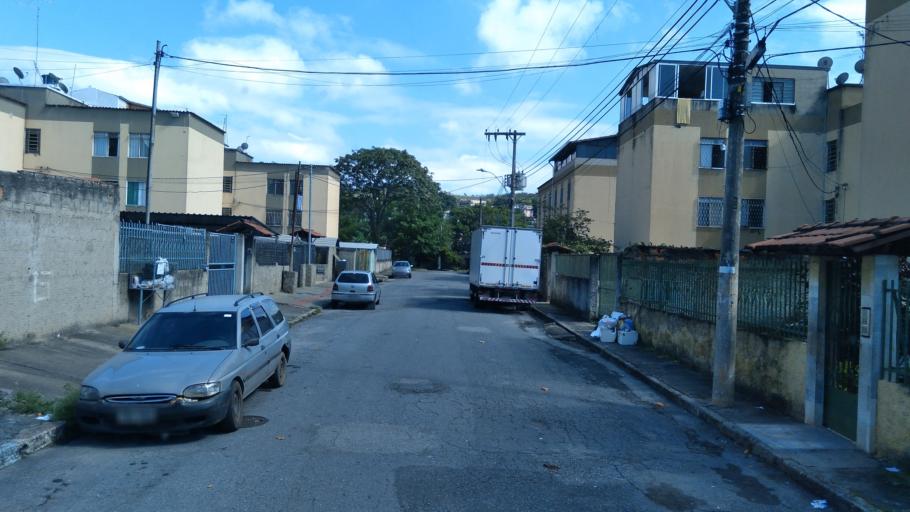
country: BR
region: Minas Gerais
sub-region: Santa Luzia
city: Santa Luzia
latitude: -19.8224
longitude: -43.9001
